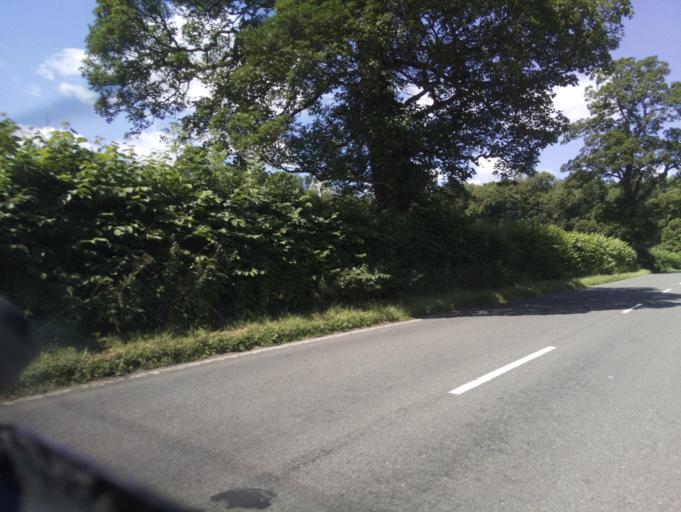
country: GB
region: England
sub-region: Derbyshire
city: Ashbourne
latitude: 53.0533
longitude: -1.7419
